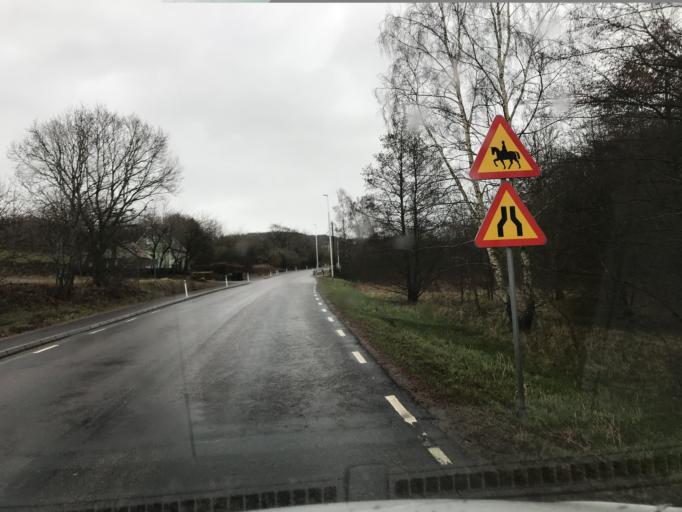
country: SE
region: Skane
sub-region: Bastads Kommun
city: Forslov
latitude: 56.3525
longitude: 12.8385
